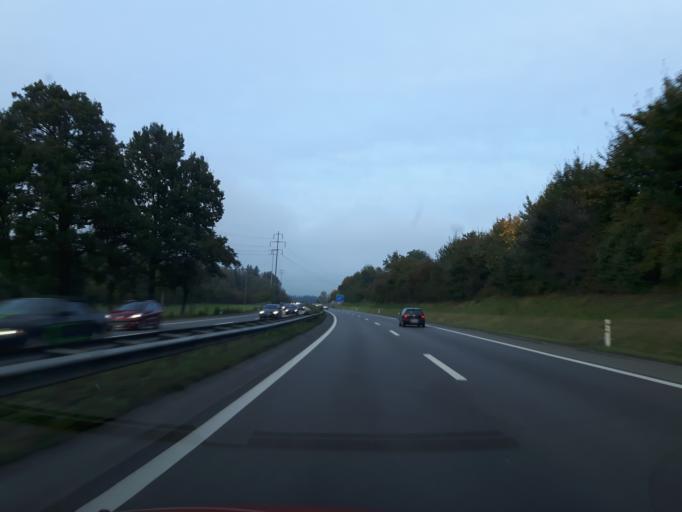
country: CH
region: Lucerne
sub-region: Lucerne-Land District
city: Buchrain
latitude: 47.0952
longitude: 8.3376
